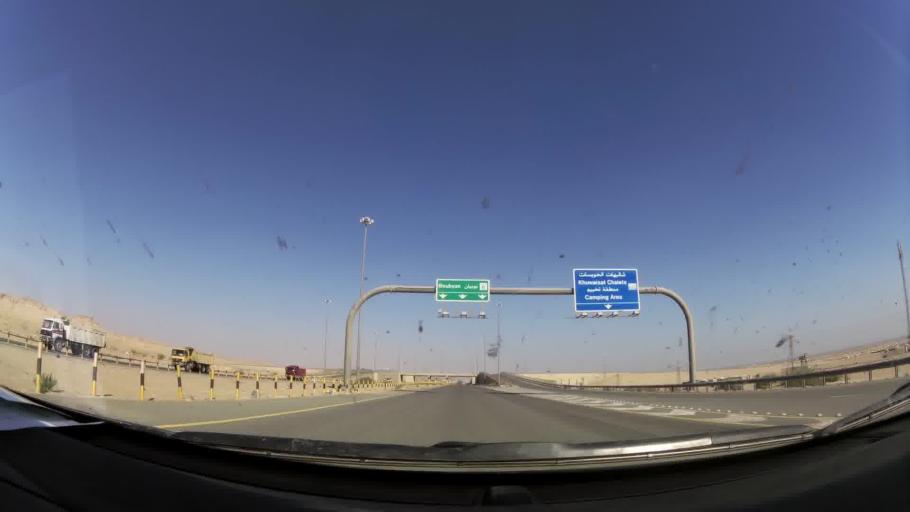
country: KW
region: Muhafazat al Jahra'
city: Al Jahra'
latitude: 29.4346
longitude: 47.7345
